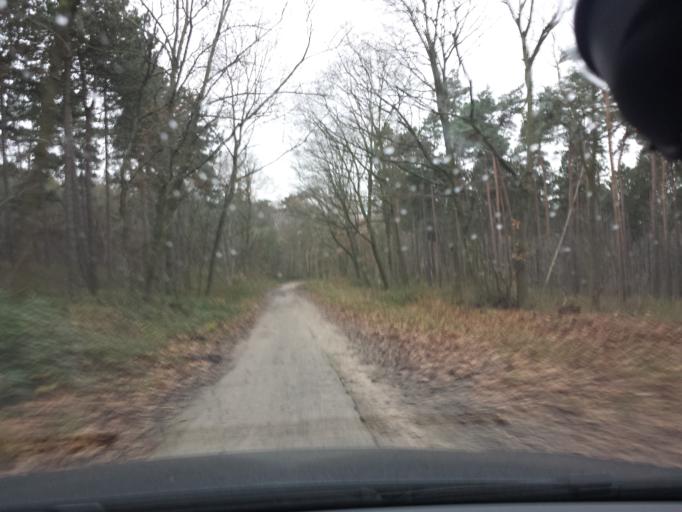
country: NL
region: Limburg
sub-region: Gemeente Brunssum
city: Brunssum
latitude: 50.9210
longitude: 6.0101
